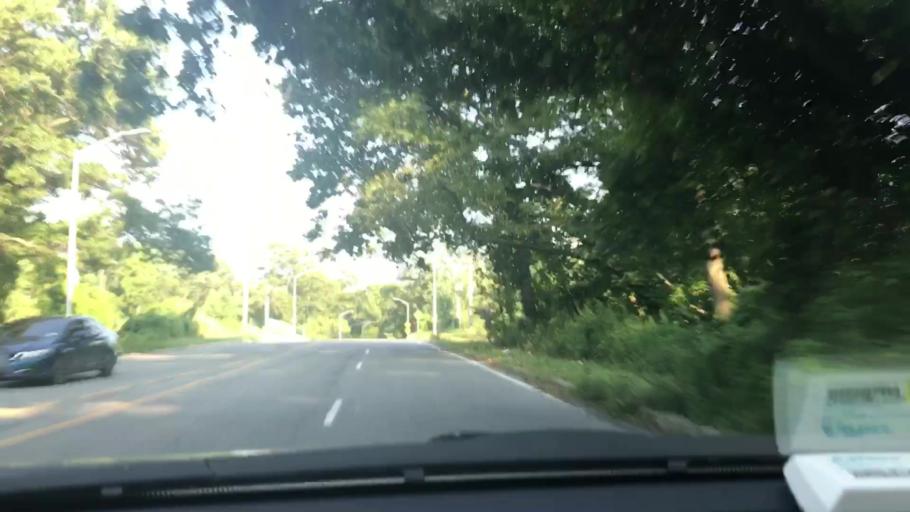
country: US
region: New York
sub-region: Bronx
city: Eastchester
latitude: 40.8709
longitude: -73.8151
